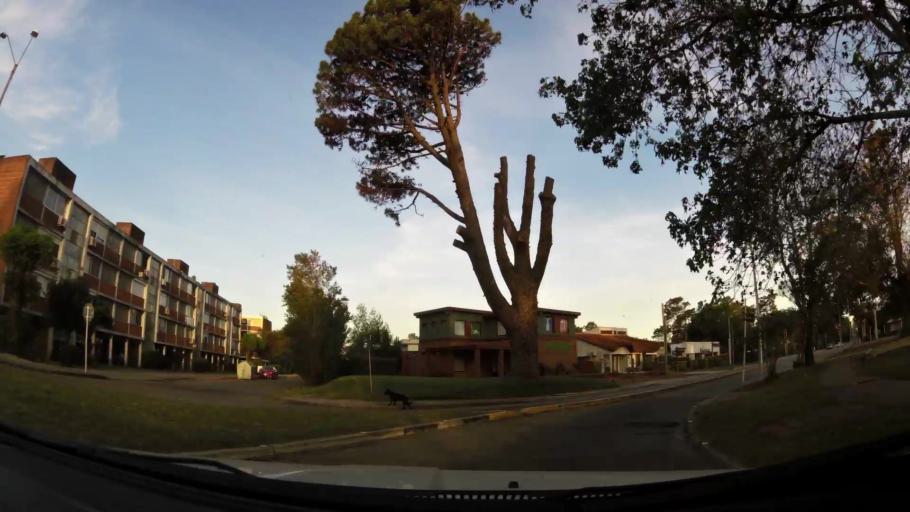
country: UY
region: Maldonado
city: Maldonado
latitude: -34.9152
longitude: -54.9526
